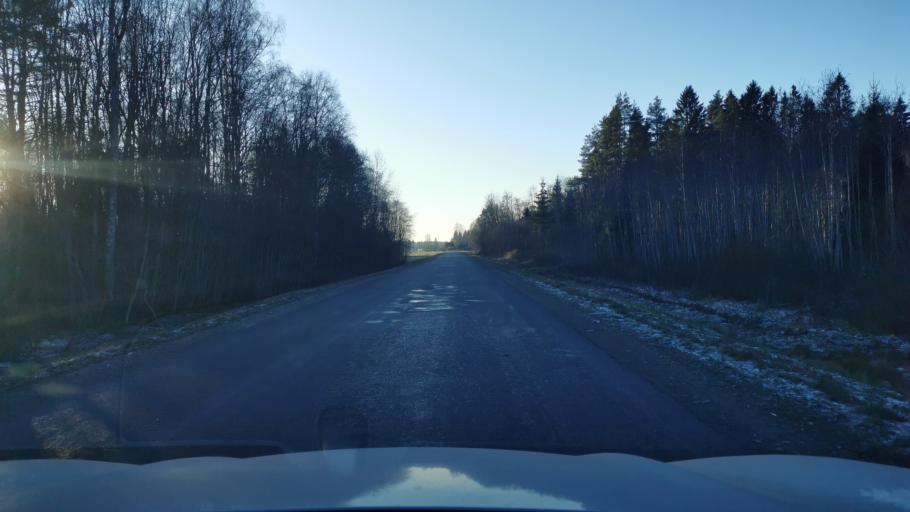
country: EE
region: Ida-Virumaa
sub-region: Kivioli linn
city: Kivioli
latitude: 59.3132
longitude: 27.0030
